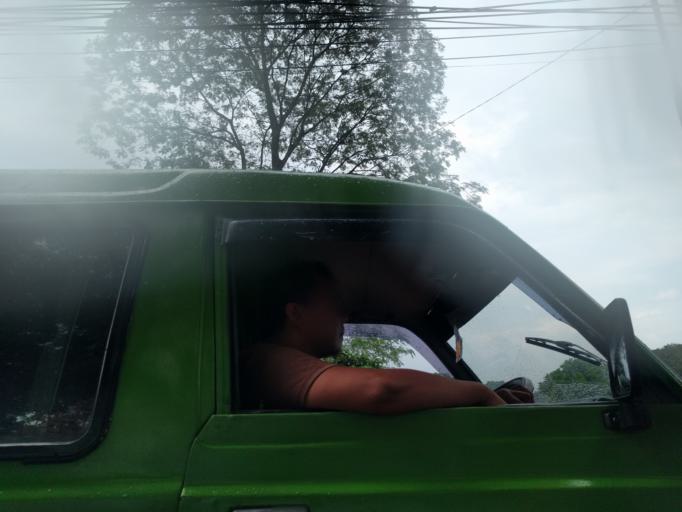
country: ID
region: West Java
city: Bogor
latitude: -6.5923
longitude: 106.8008
